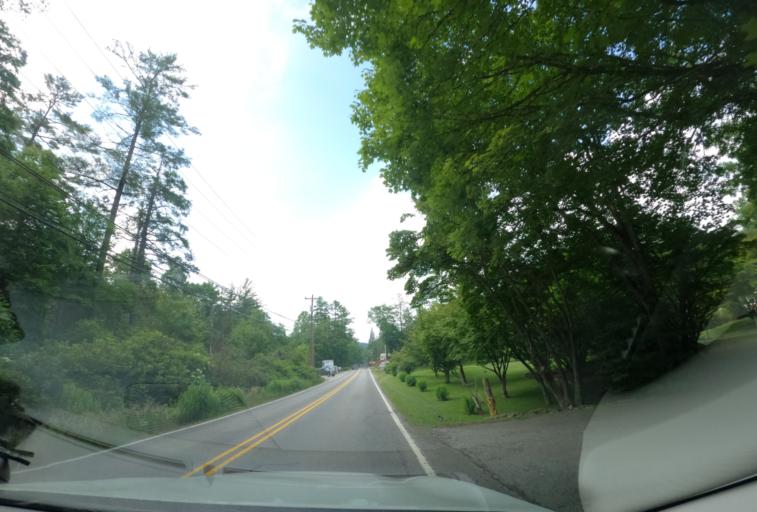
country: US
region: North Carolina
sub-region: Macon County
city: Franklin
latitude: 35.0770
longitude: -83.1898
